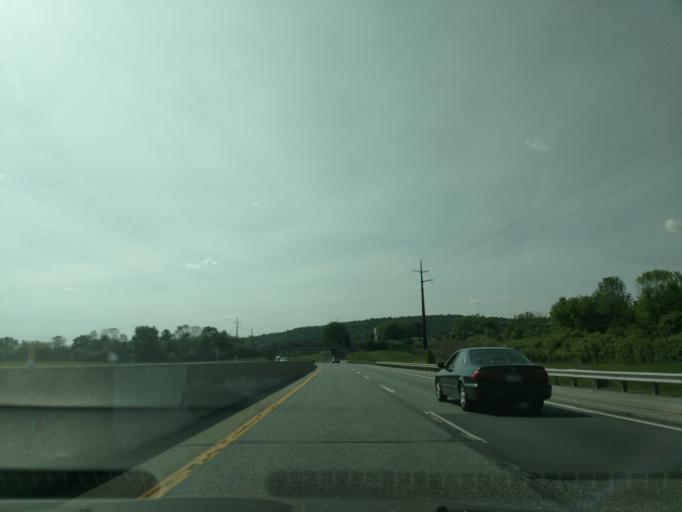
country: US
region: Pennsylvania
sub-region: Lancaster County
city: Swartzville
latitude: 40.2227
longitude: -76.0931
